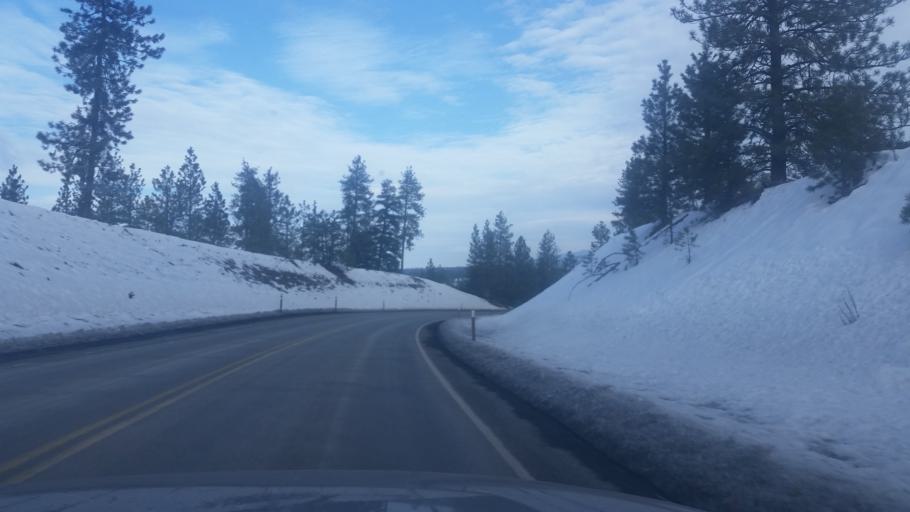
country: US
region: Washington
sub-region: Spokane County
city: Fairchild Air Force Base
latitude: 47.8387
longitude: -117.8695
